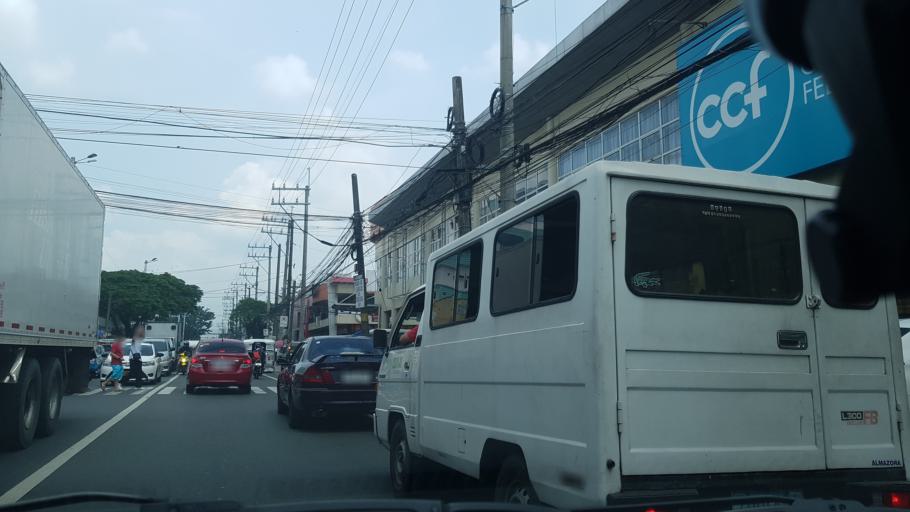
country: PH
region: Calabarzon
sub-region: Province of Rizal
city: San Mateo
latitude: 14.6695
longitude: 121.1083
